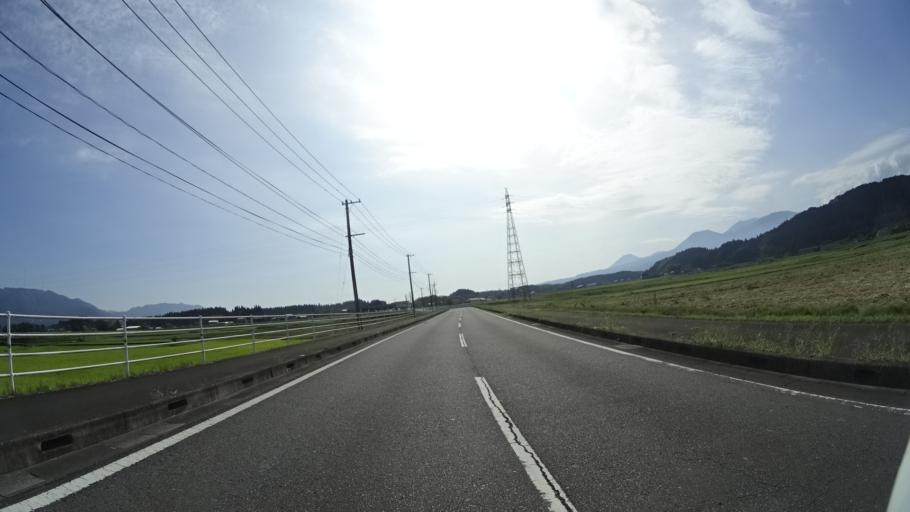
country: JP
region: Kagoshima
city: Okuchi-shinohara
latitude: 32.0424
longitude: 130.7824
